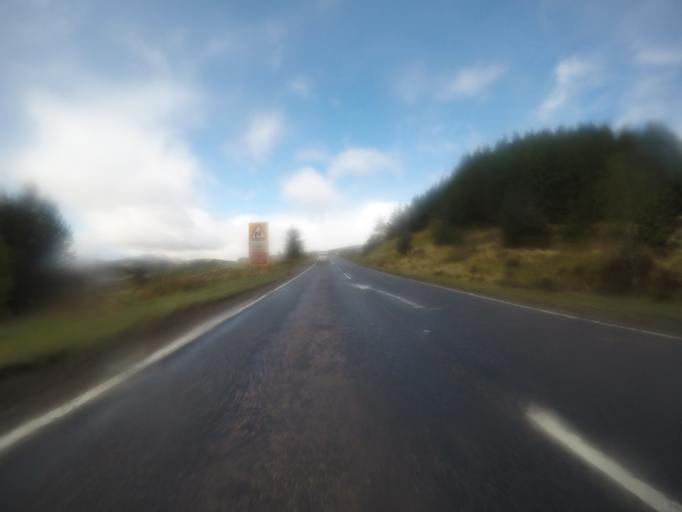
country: GB
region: Scotland
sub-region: Highland
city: Spean Bridge
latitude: 57.0837
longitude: -4.9590
